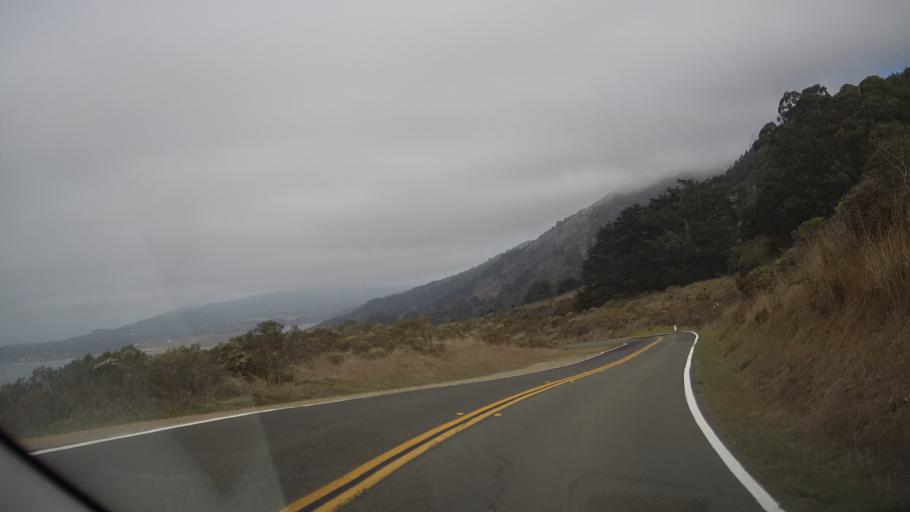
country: US
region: California
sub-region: Marin County
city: Bolinas
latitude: 37.8925
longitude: -122.6254
